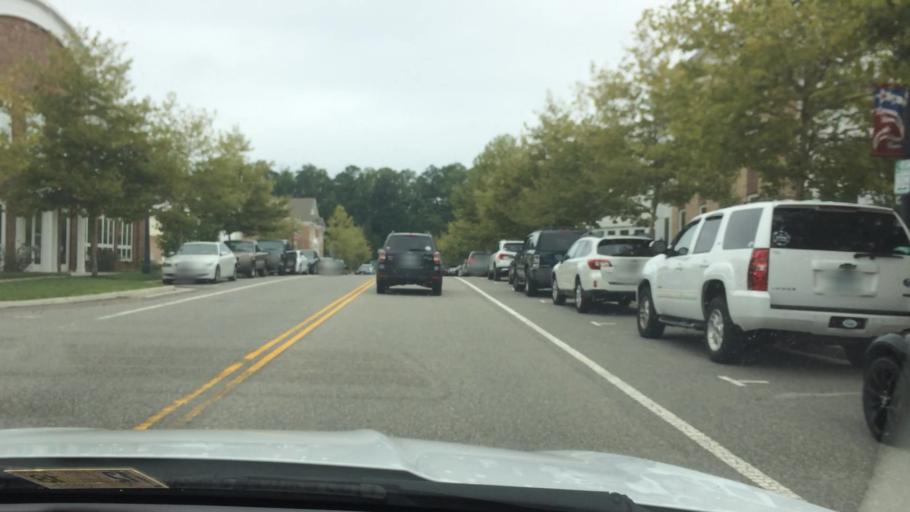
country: US
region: Virginia
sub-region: James City County
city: Williamsburg
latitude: 37.2838
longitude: -76.7429
